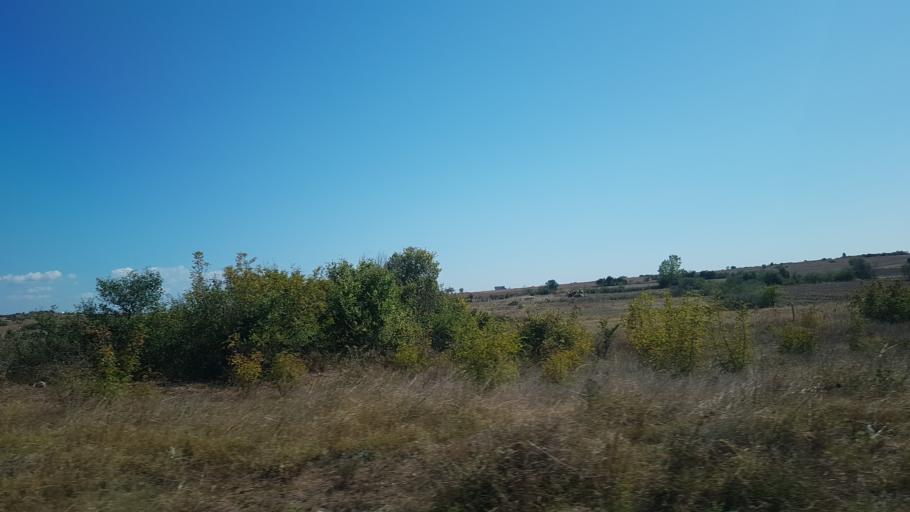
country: TR
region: Kirklareli
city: Kirklareli
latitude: 41.7661
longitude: 27.2238
